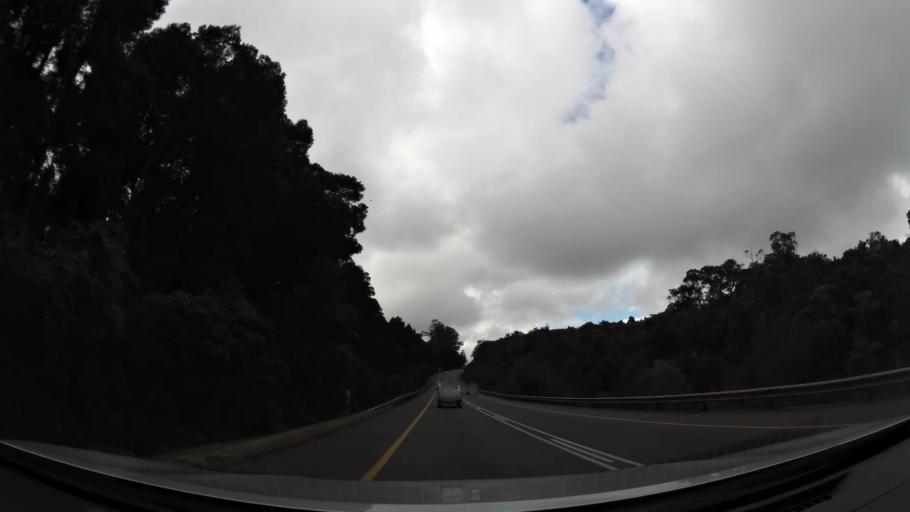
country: ZA
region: Western Cape
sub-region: Eden District Municipality
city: Knysna
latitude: -34.0370
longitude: 23.2060
